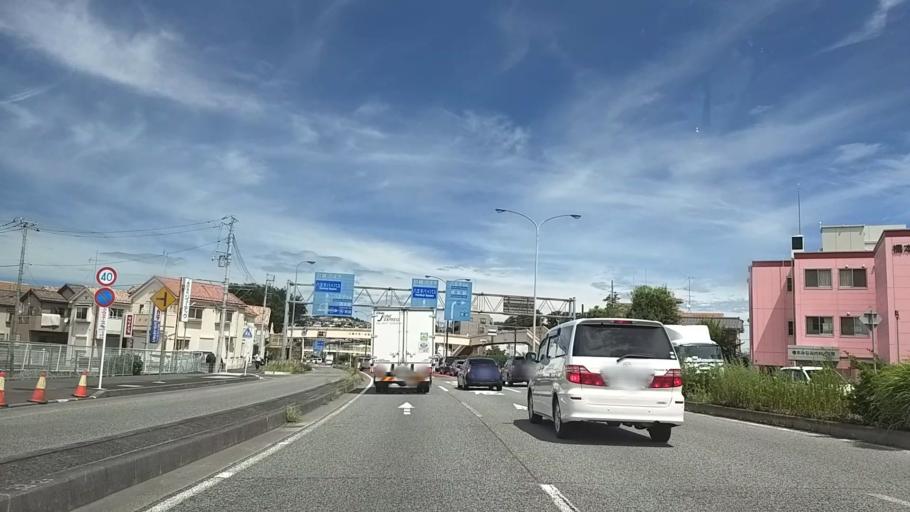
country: JP
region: Tokyo
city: Hachioji
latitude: 35.6004
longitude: 139.3389
